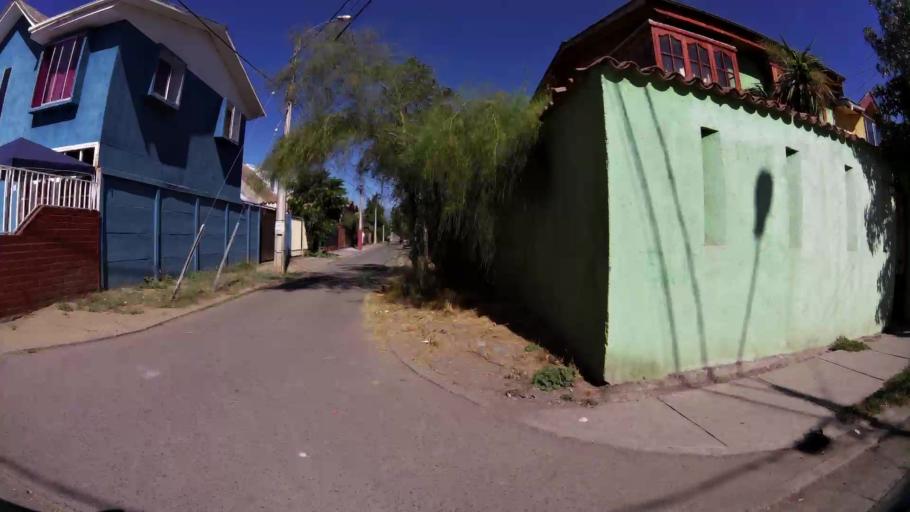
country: CL
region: O'Higgins
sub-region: Provincia de Colchagua
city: Chimbarongo
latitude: -34.5788
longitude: -71.0027
